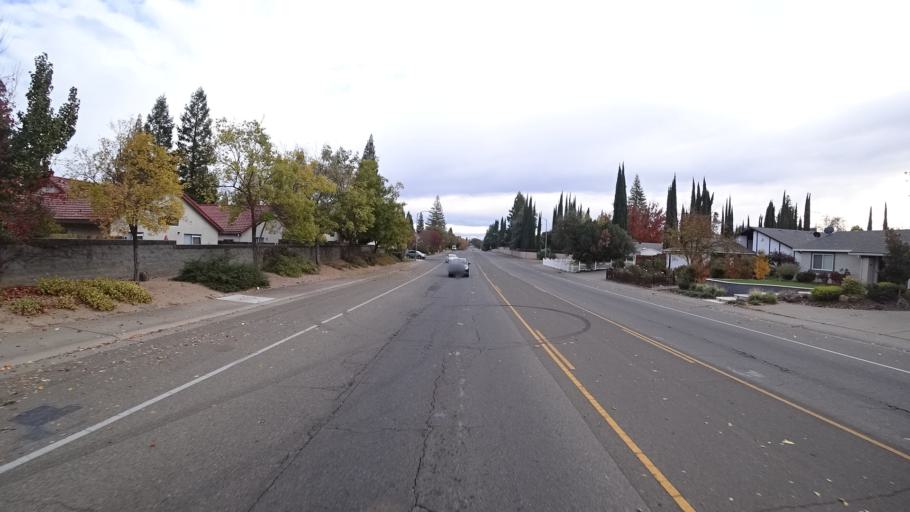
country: US
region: California
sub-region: Sacramento County
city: Citrus Heights
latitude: 38.7004
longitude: -121.2495
